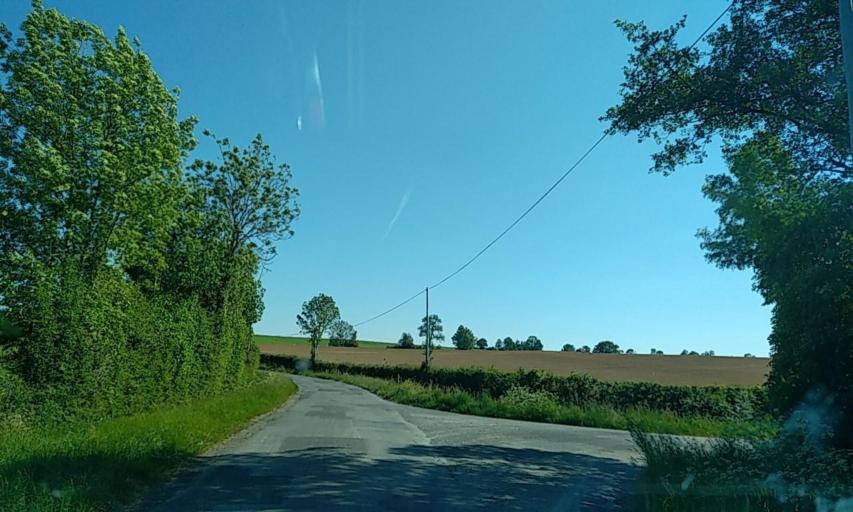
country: FR
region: Poitou-Charentes
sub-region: Departement des Deux-Sevres
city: Boisme
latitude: 46.7724
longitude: -0.4119
